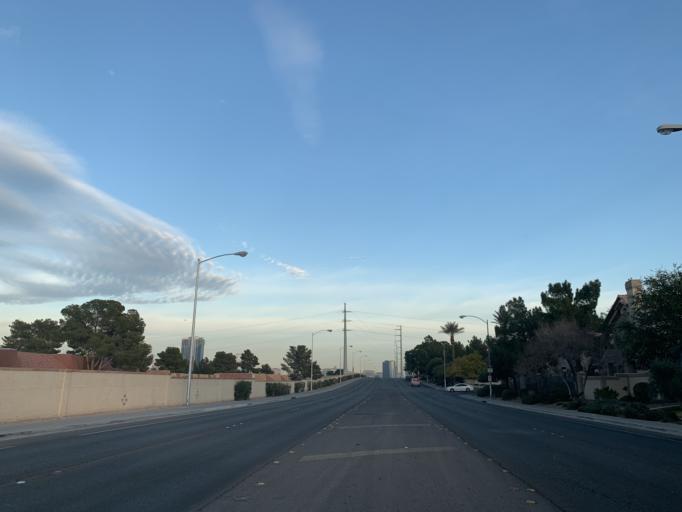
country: US
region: Nevada
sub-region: Clark County
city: Spring Valley
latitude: 36.1077
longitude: -115.2163
